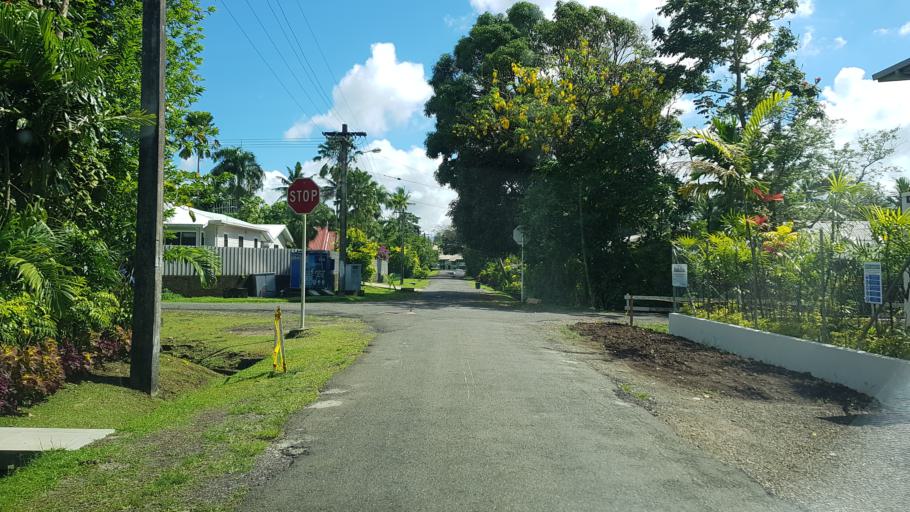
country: FJ
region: Central
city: Suva
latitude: -18.1468
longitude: 178.4549
